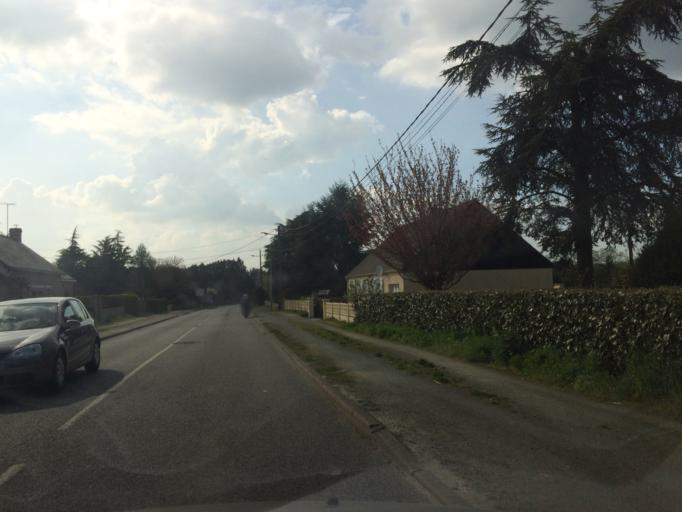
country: FR
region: Pays de la Loire
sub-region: Departement de la Loire-Atlantique
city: Blain
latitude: 47.4782
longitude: -1.7773
